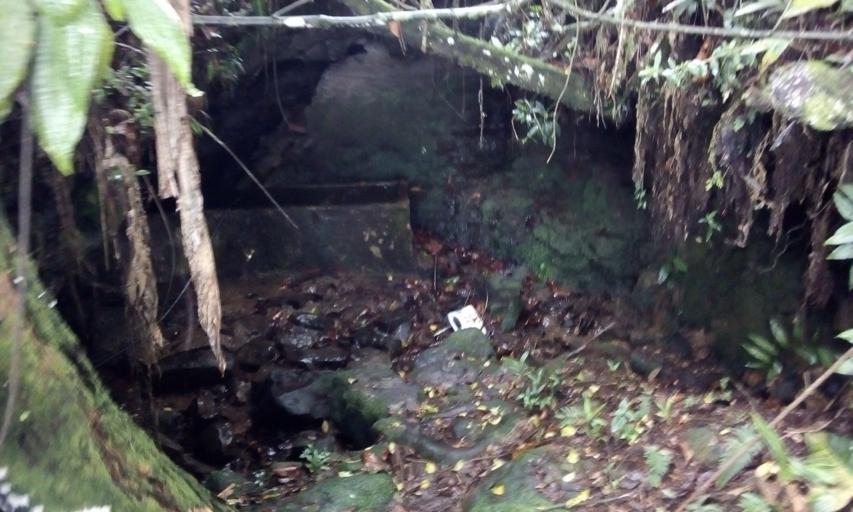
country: CO
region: Boyaca
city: Santana
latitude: 5.9987
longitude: -73.4954
